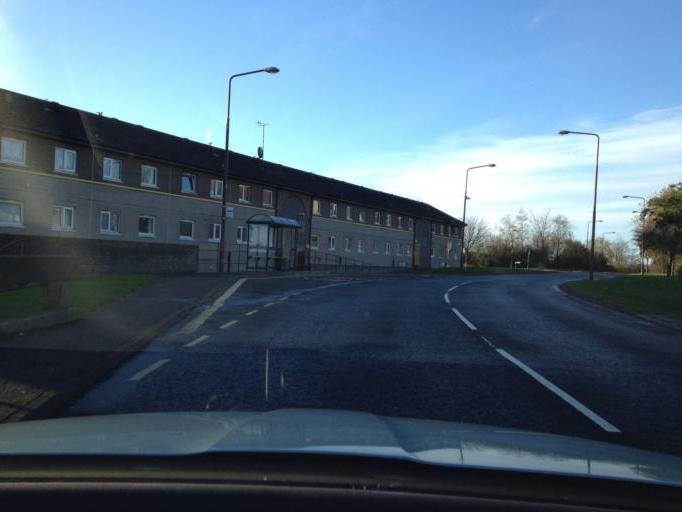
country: GB
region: Scotland
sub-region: West Lothian
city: Mid Calder
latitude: 55.8971
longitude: -3.4997
